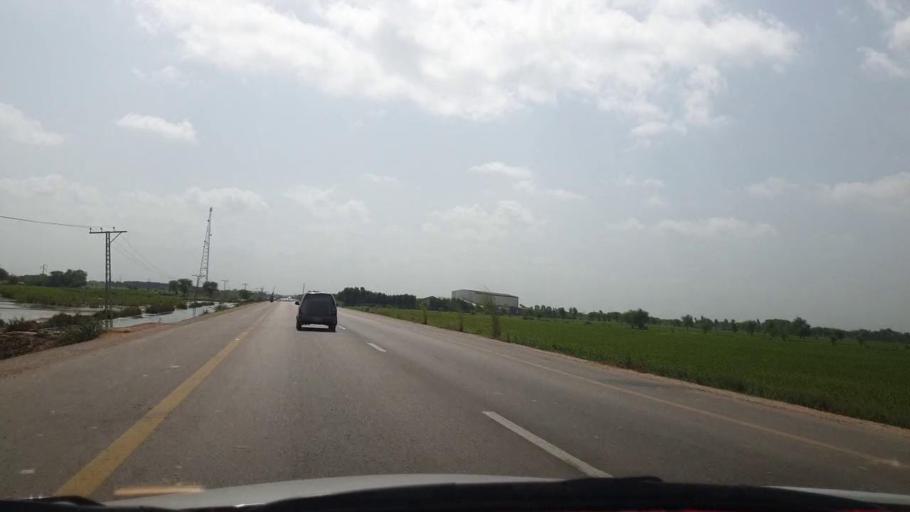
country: PK
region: Sindh
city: Matli
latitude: 24.9384
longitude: 68.7061
